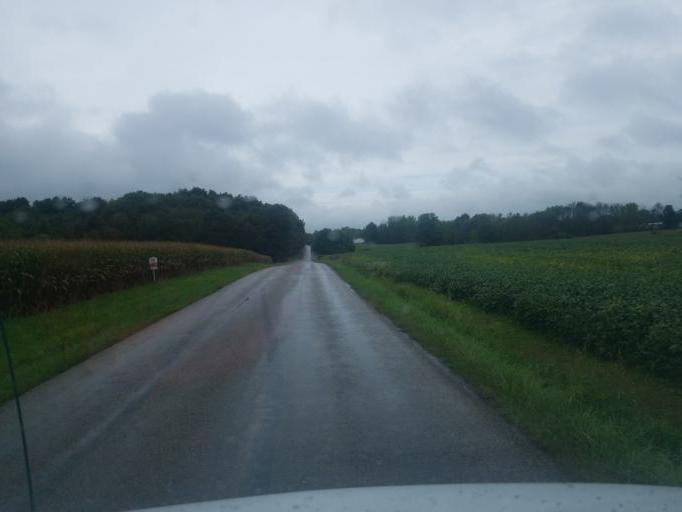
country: US
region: Ohio
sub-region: Wayne County
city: West Salem
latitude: 40.9562
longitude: -82.1117
